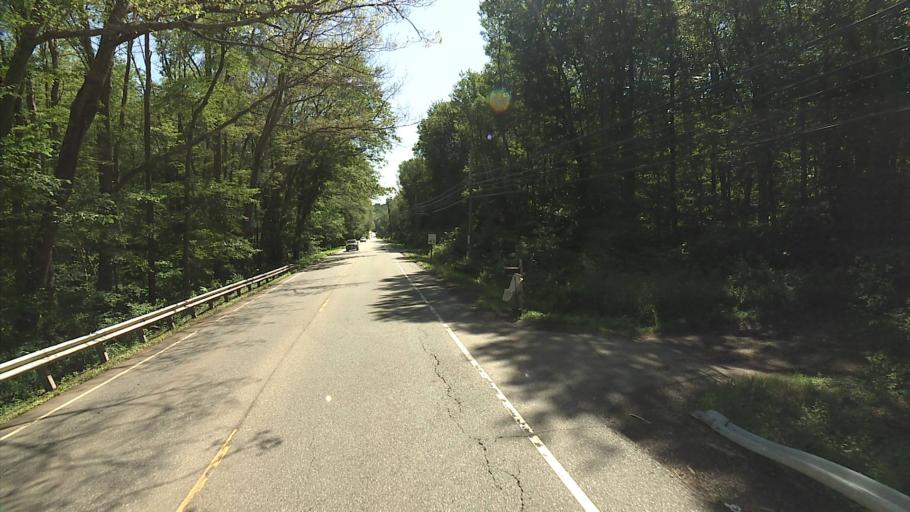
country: US
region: Connecticut
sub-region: New London County
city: Colchester
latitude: 41.5571
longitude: -72.3735
